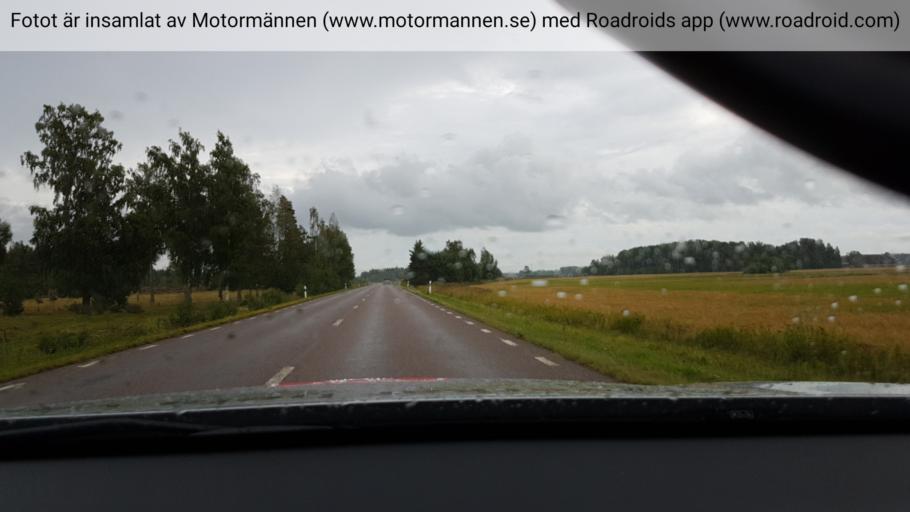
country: SE
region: Uppsala
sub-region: Tierps Kommun
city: Karlholmsbruk
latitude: 60.4923
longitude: 17.7126
